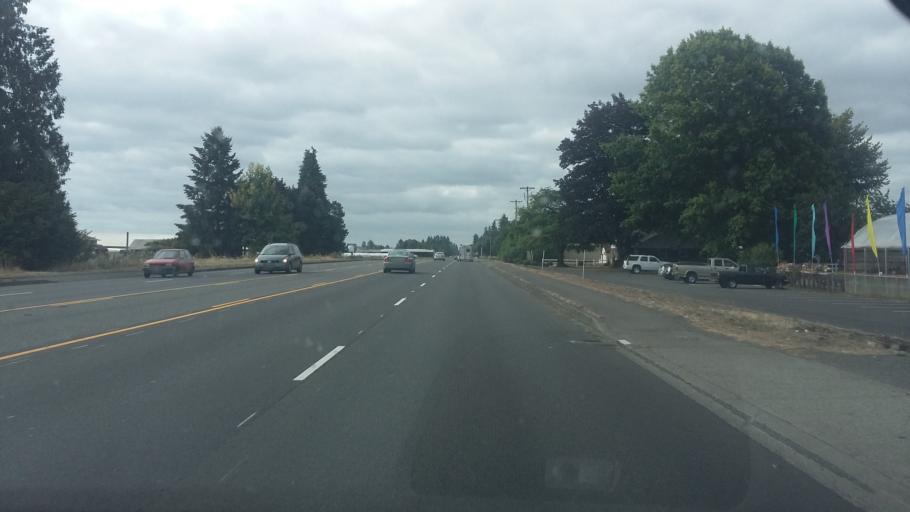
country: US
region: Washington
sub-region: Clark County
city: Brush Prairie
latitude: 45.7245
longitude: -122.5526
